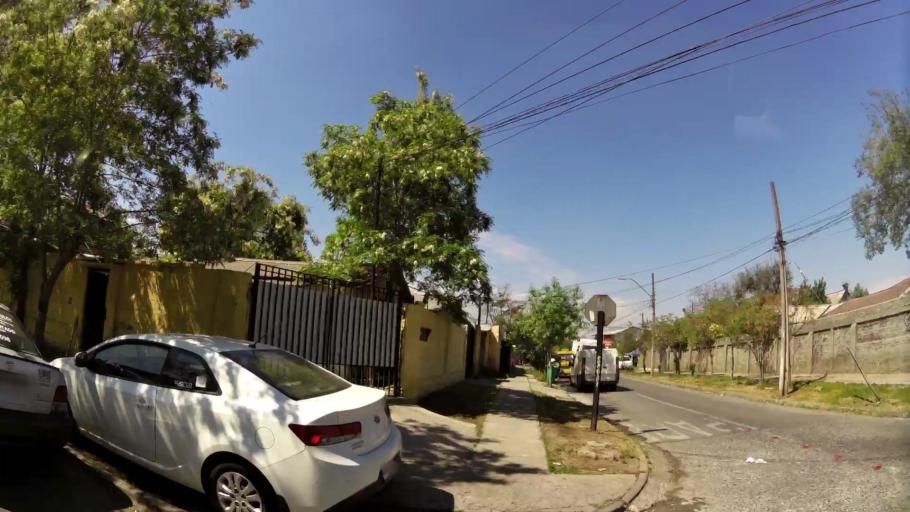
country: CL
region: Santiago Metropolitan
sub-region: Provincia de Santiago
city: La Pintana
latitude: -33.5291
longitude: -70.6548
